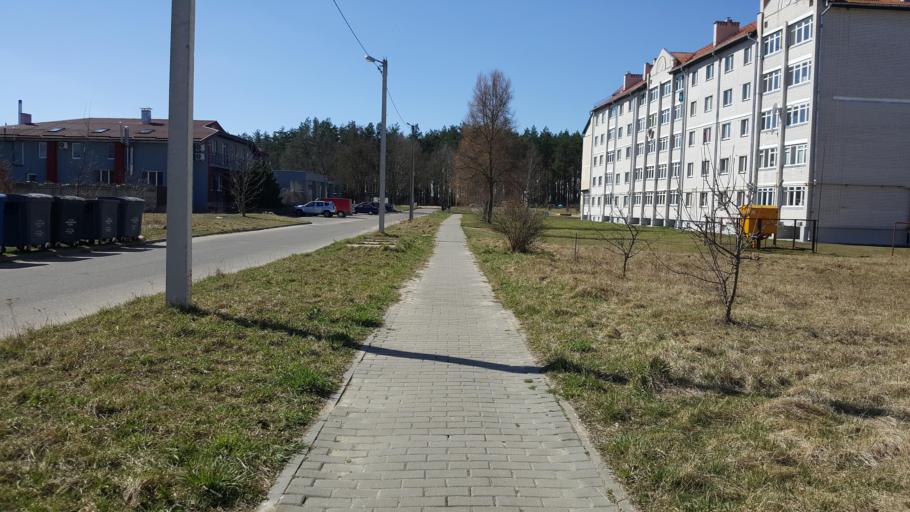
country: BY
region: Brest
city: Kamyanyets
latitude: 52.3902
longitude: 23.8254
